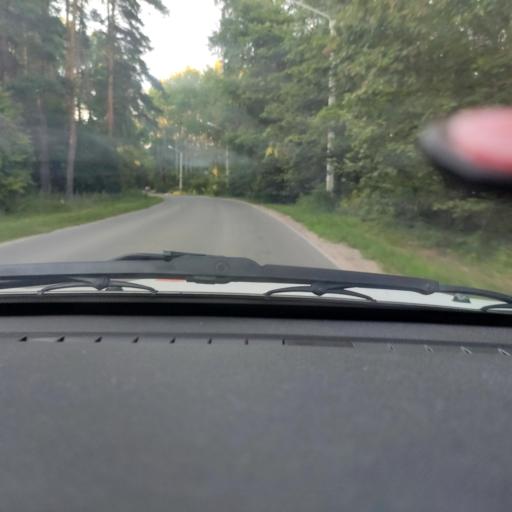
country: RU
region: Voronezj
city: Ramon'
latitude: 51.8940
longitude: 39.2819
